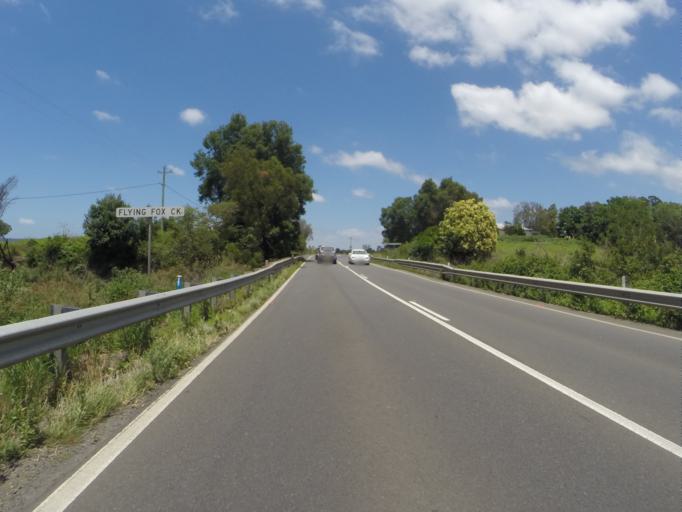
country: AU
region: New South Wales
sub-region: Shoalhaven Shire
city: Berry
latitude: -34.7949
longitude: 150.6698
